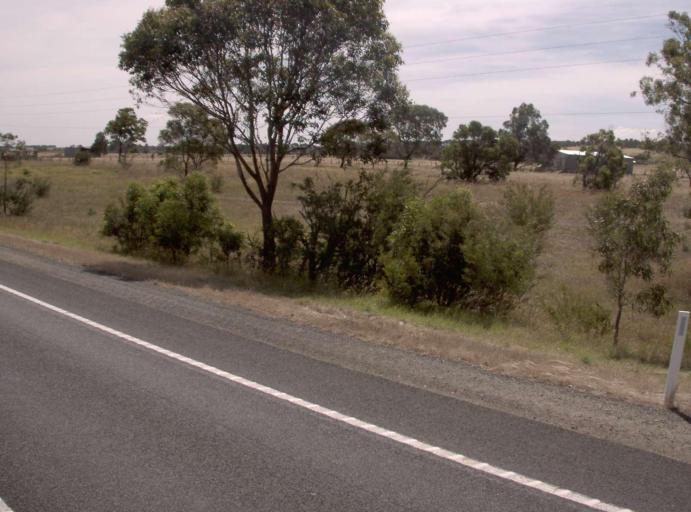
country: AU
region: Victoria
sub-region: Wellington
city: Heyfield
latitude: -38.1326
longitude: 146.8113
